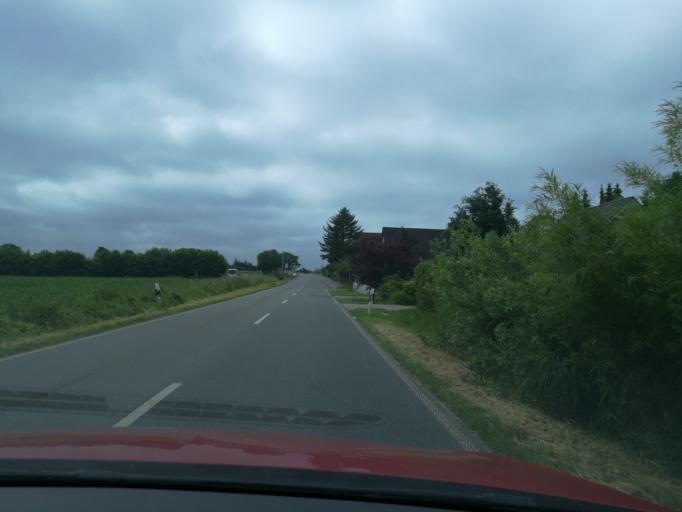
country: DE
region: Schleswig-Holstein
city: Politz
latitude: 53.7788
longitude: 10.3744
